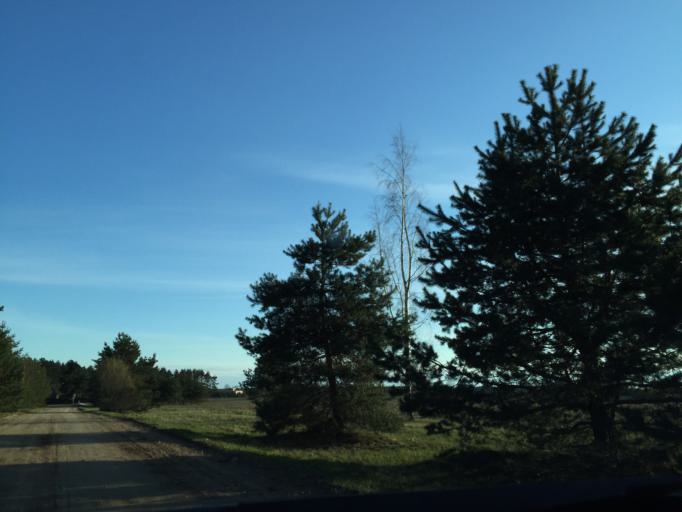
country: LV
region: Kekava
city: Kekava
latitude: 56.8710
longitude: 24.2005
